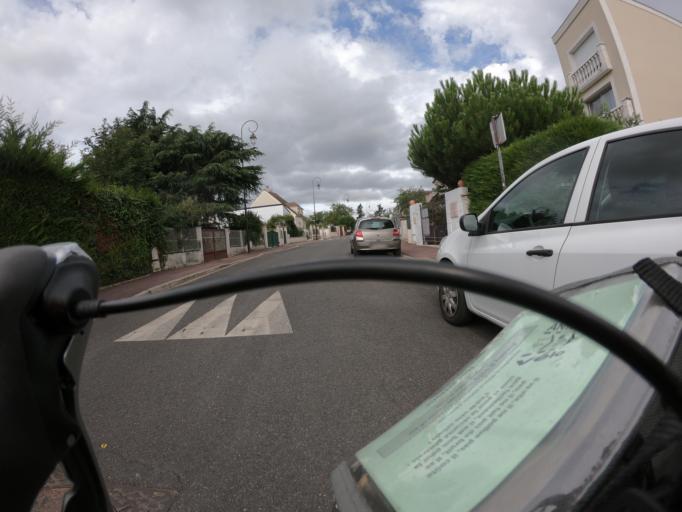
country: FR
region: Ile-de-France
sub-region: Departement de l'Essonne
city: Verrieres-le-Buisson
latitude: 48.7558
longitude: 2.2781
